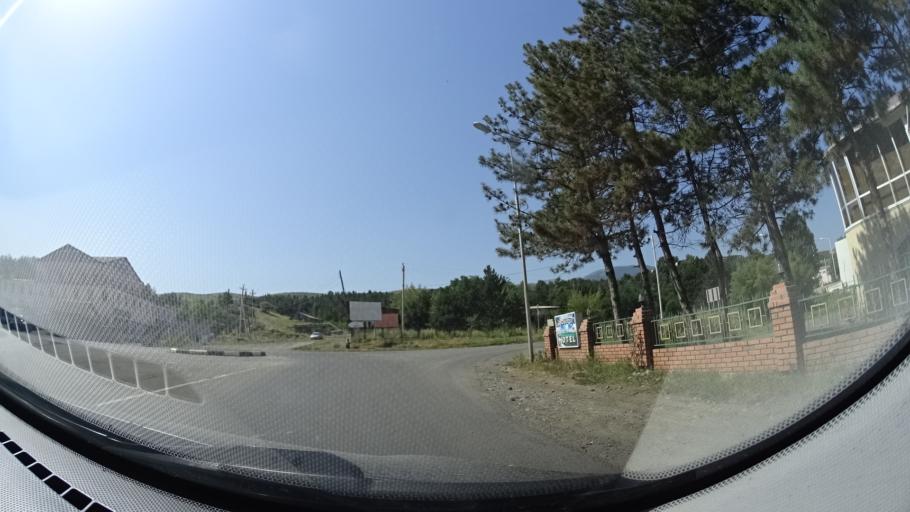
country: GE
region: Samtskhe-Javakheti
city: Akhaltsikhe
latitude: 41.6398
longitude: 43.0147
